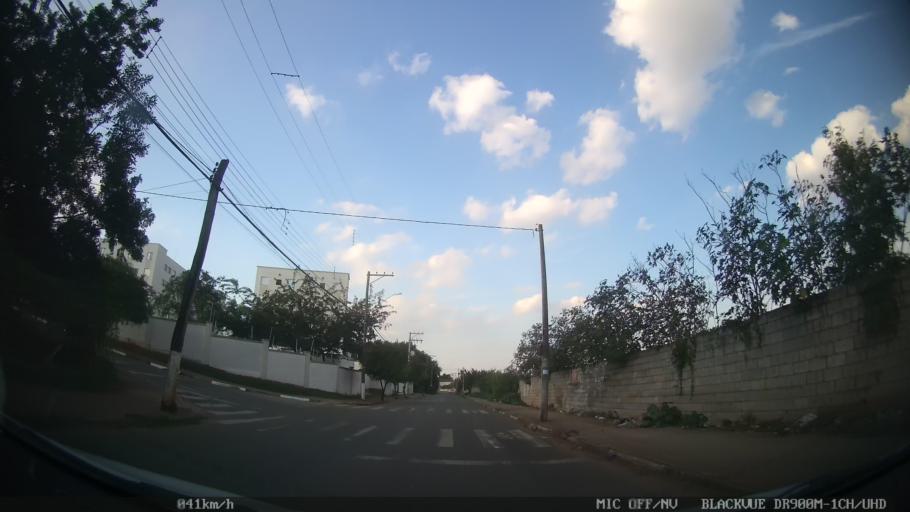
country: BR
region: Sao Paulo
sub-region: Hortolandia
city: Hortolandia
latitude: -22.8673
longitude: -47.1436
